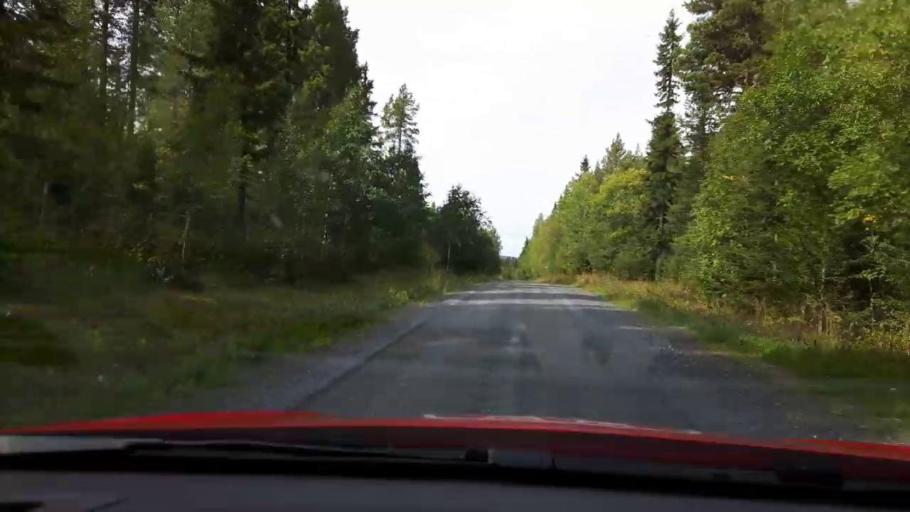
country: SE
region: Jaemtland
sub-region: Krokoms Kommun
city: Valla
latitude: 63.2593
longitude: 13.8104
